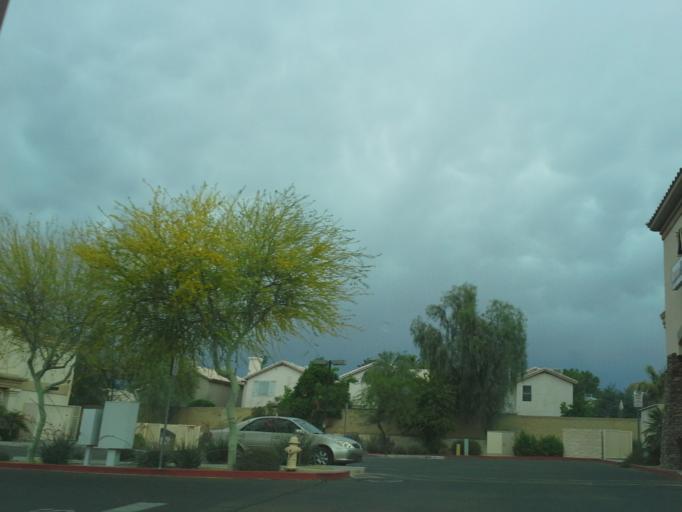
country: US
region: Arizona
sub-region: Maricopa County
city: Paradise Valley
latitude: 33.6416
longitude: -111.9951
